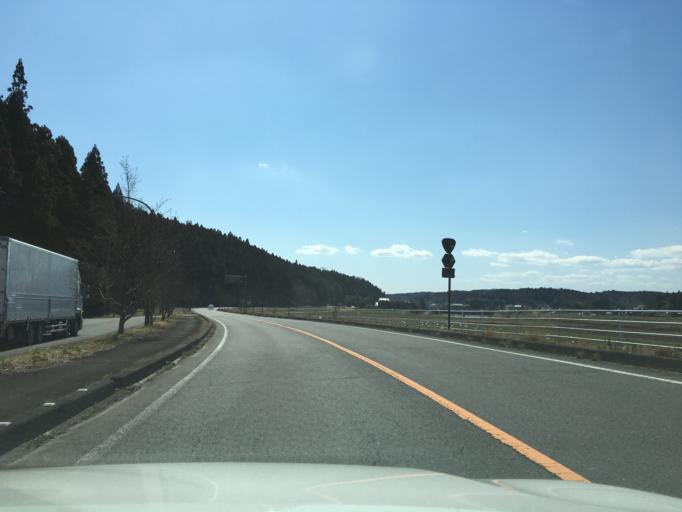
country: JP
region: Tochigi
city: Kuroiso
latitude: 36.9493
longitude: 140.1483
